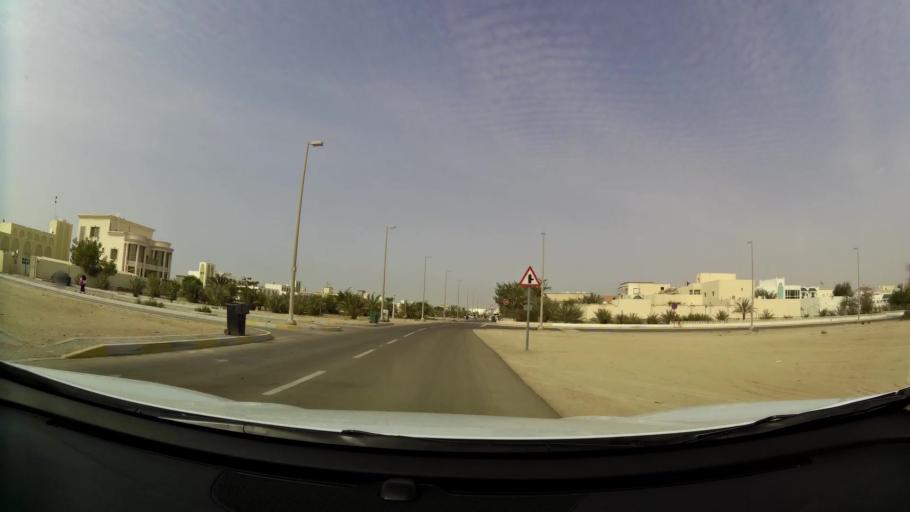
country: AE
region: Abu Dhabi
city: Abu Dhabi
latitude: 24.5767
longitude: 54.6870
